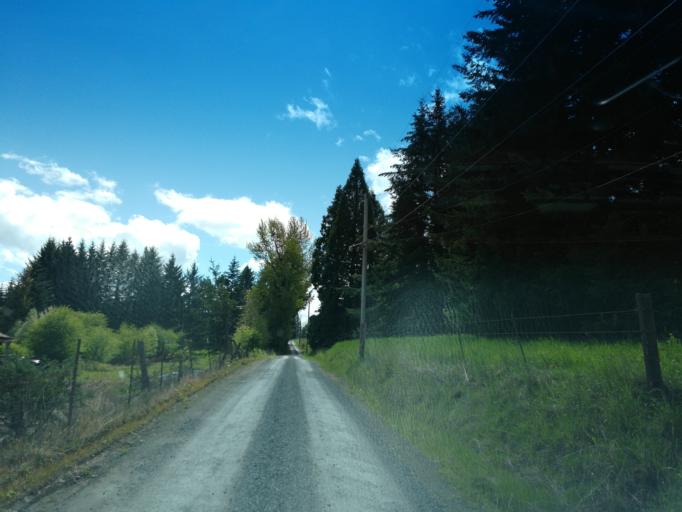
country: US
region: Oregon
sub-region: Clackamas County
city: Damascus
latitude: 45.4496
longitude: -122.4486
